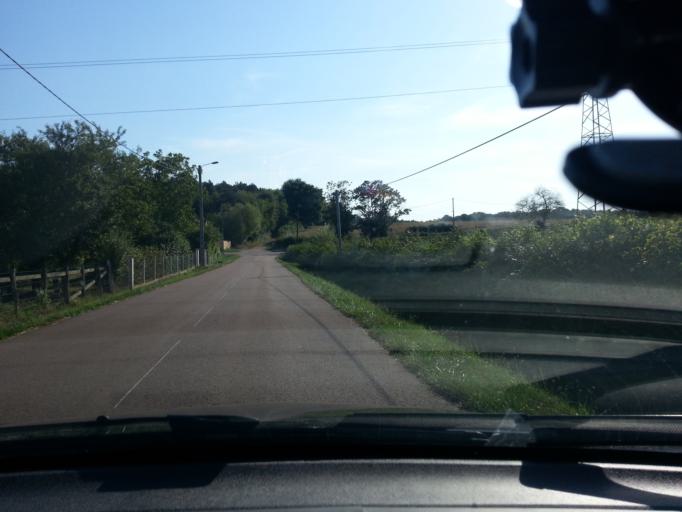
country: FR
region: Bourgogne
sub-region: Departement de Saone-et-Loire
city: Saint-Remy
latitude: 46.7604
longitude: 4.8129
